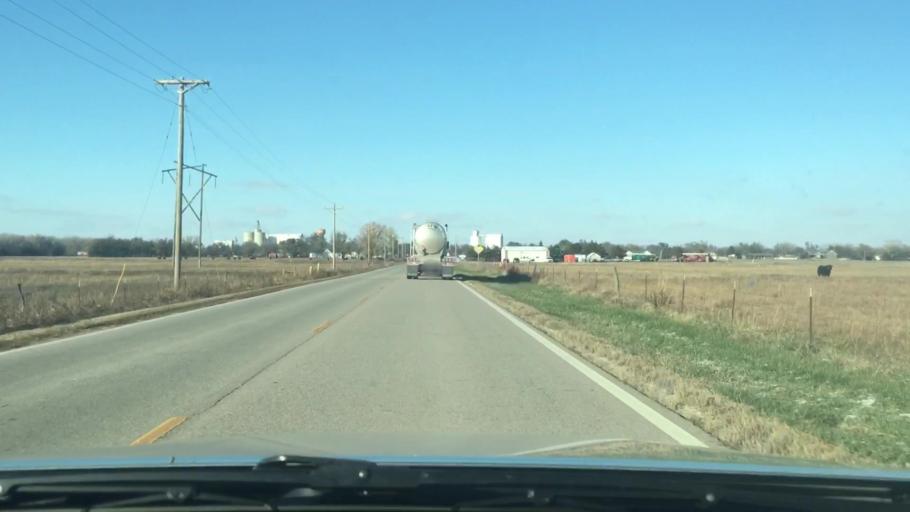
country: US
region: Kansas
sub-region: Rice County
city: Sterling
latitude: 38.1950
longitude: -98.2068
